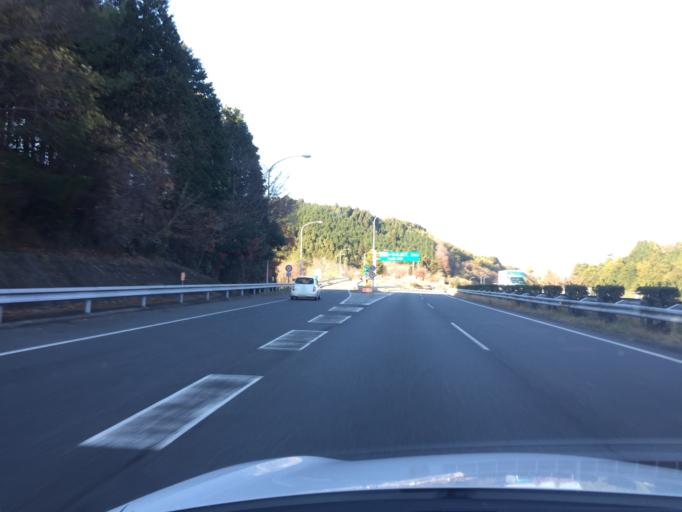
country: JP
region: Fukushima
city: Iwaki
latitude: 37.0174
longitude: 140.8134
